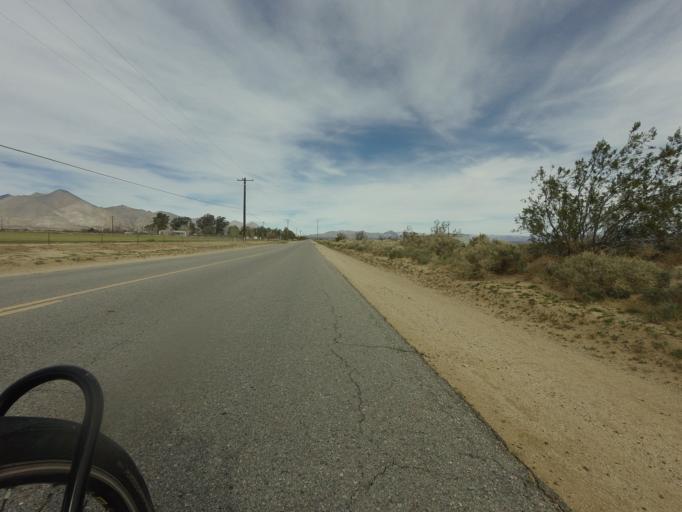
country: US
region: California
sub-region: Kern County
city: Inyokern
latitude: 35.7458
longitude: -117.8417
